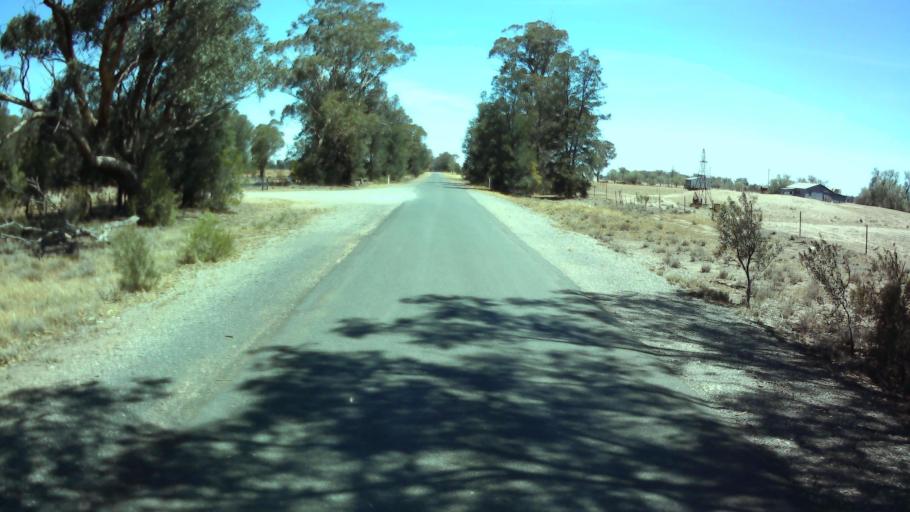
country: AU
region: New South Wales
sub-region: Weddin
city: Grenfell
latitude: -33.9029
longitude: 147.6860
